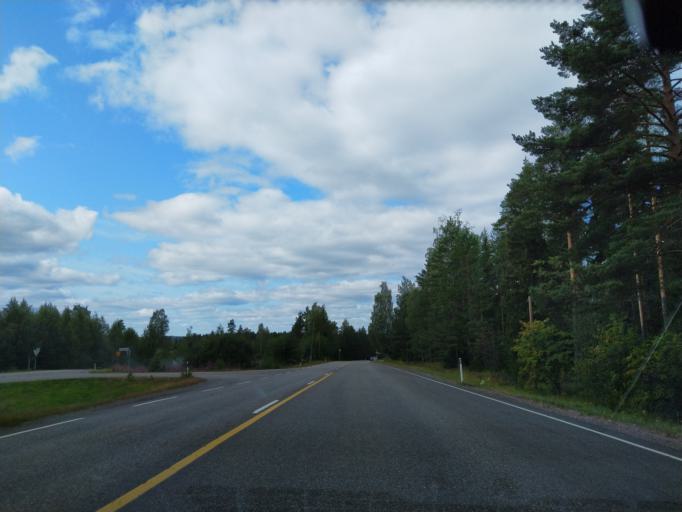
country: FI
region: Haeme
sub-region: Riihimaeki
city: Loppi
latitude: 60.7250
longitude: 24.4146
